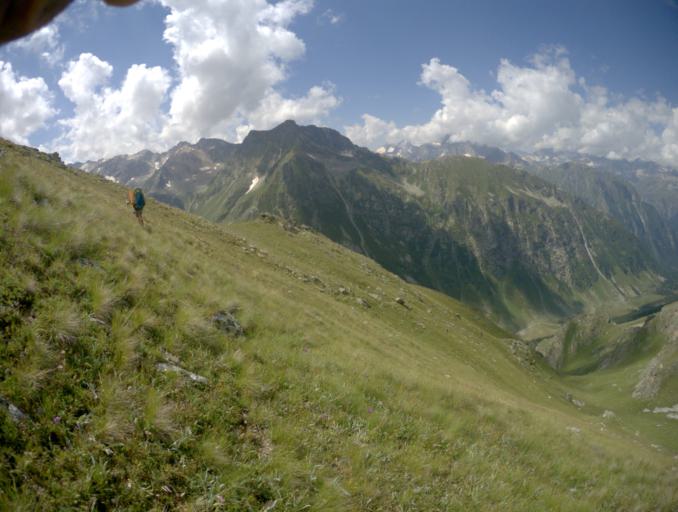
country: RU
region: Karachayevo-Cherkesiya
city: Uchkulan
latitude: 43.2971
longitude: 42.0685
